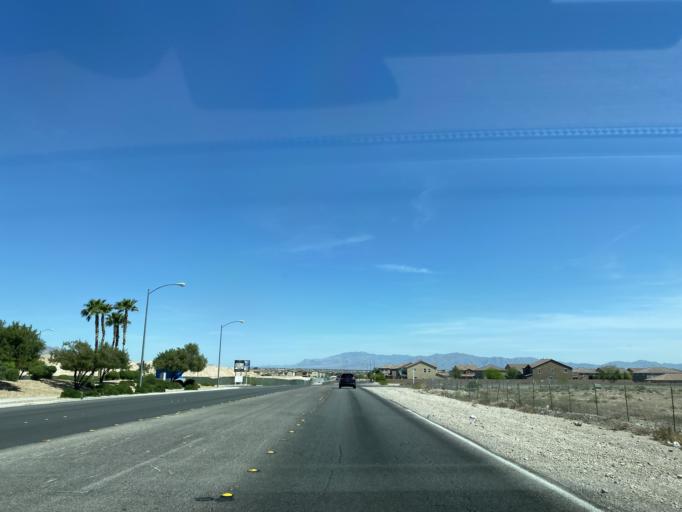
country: US
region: Nevada
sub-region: Clark County
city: Spring Valley
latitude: 36.0728
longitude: -115.2607
